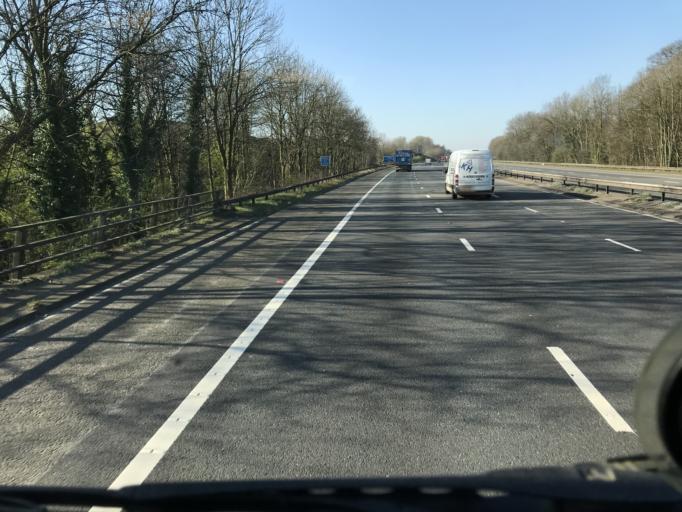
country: GB
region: England
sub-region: Borough of Halton
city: Daresbury
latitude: 53.3170
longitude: -2.6608
